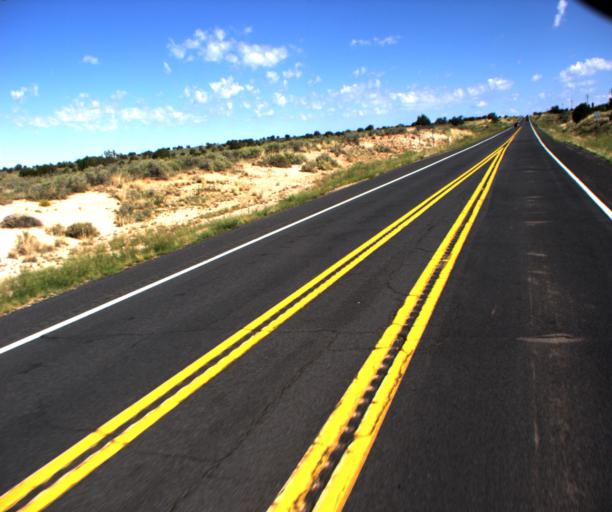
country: US
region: Arizona
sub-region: Coconino County
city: Grand Canyon Village
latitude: 35.7316
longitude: -112.1311
